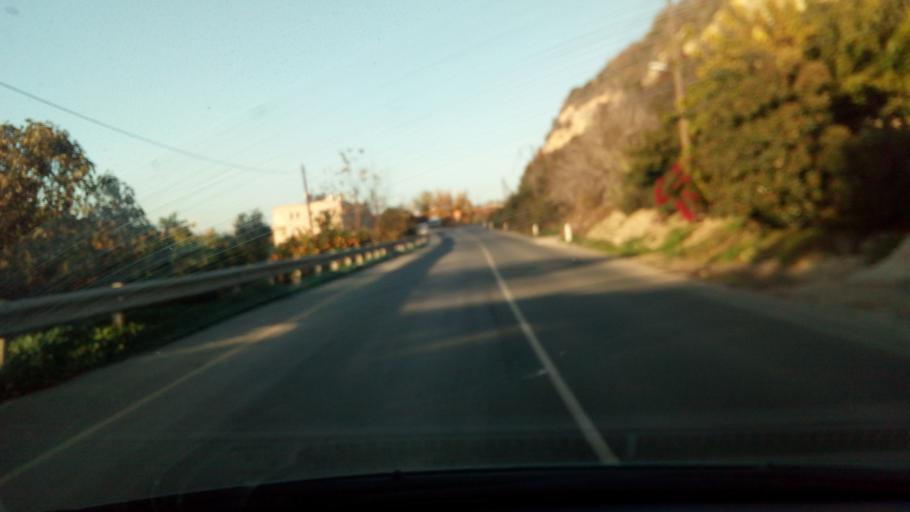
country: CY
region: Pafos
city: Polis
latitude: 34.9782
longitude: 32.4500
